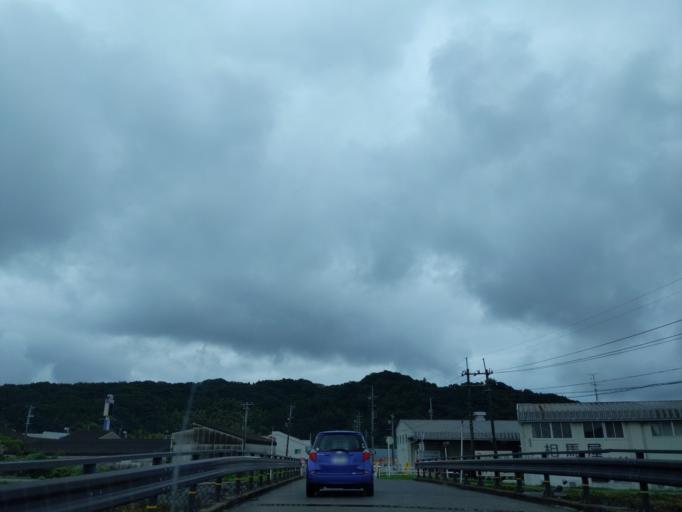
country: JP
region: Fukushima
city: Iwaki
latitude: 36.9690
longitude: 140.8889
